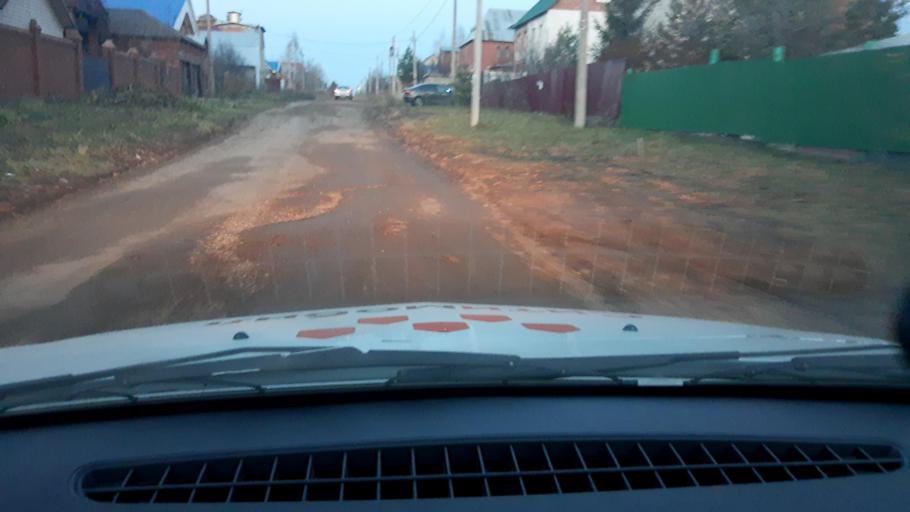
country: RU
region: Bashkortostan
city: Iglino
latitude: 54.7778
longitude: 56.2341
